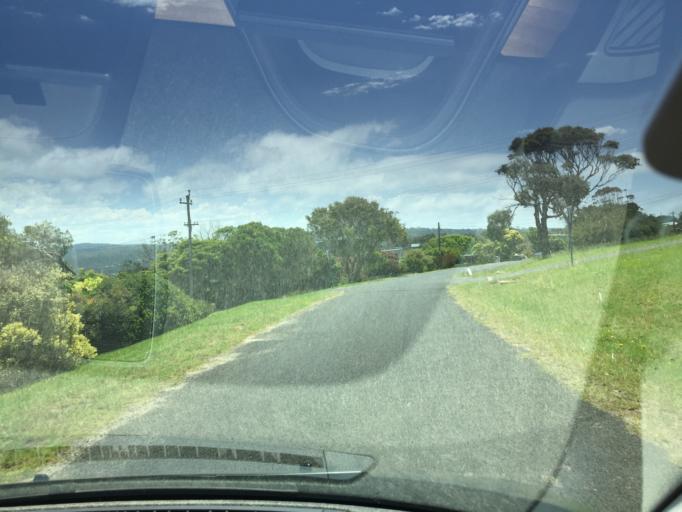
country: AU
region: New South Wales
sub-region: Bega Valley
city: Merimbula
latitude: -36.8944
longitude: 149.9263
